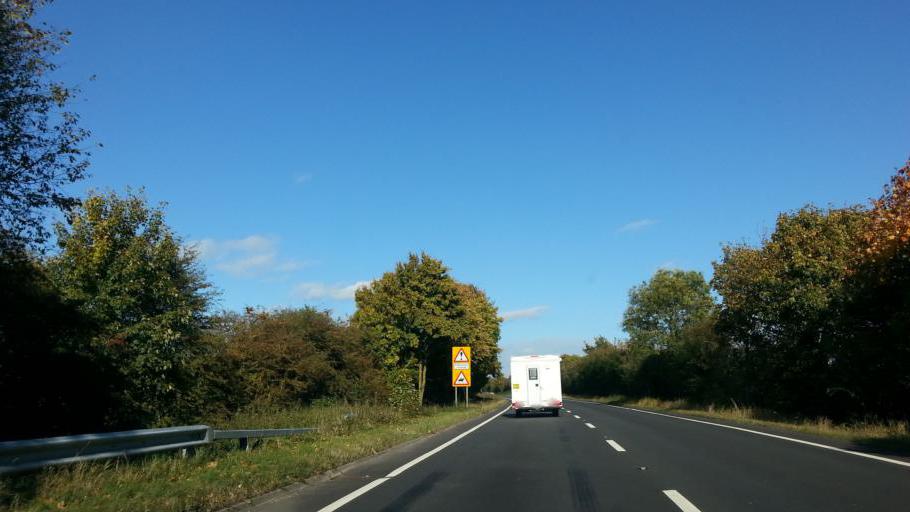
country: GB
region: England
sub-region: Northamptonshire
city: Oundle
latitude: 52.4716
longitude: -0.4575
